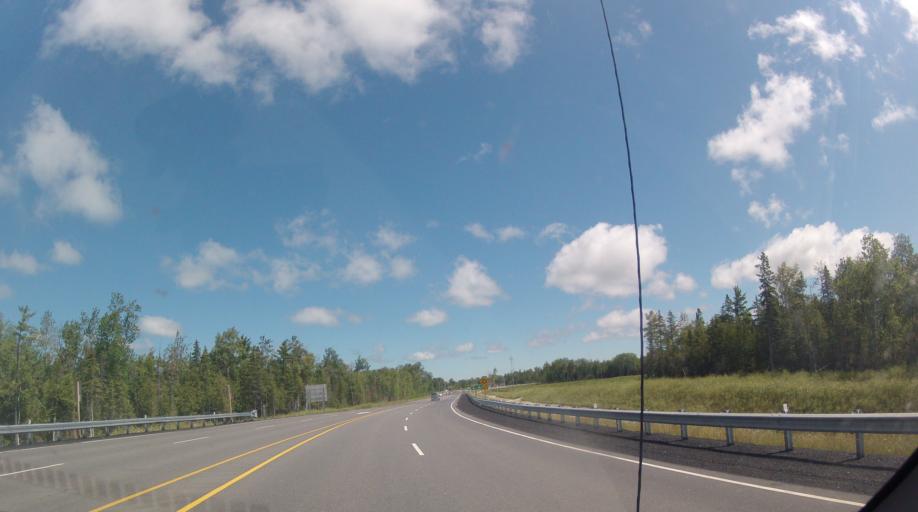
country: CA
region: Ontario
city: Collingwood
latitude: 44.4635
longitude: -80.1120
